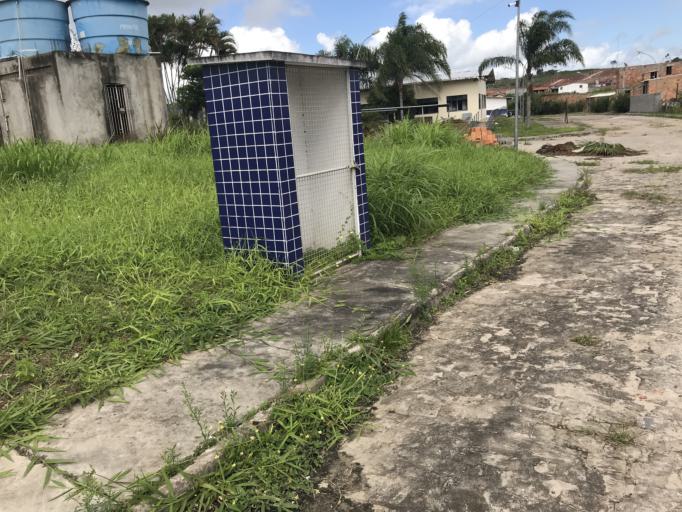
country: BR
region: Bahia
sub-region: Santo Antonio De Jesus
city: Santo Antonio de Jesus
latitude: -12.9790
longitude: -39.2818
